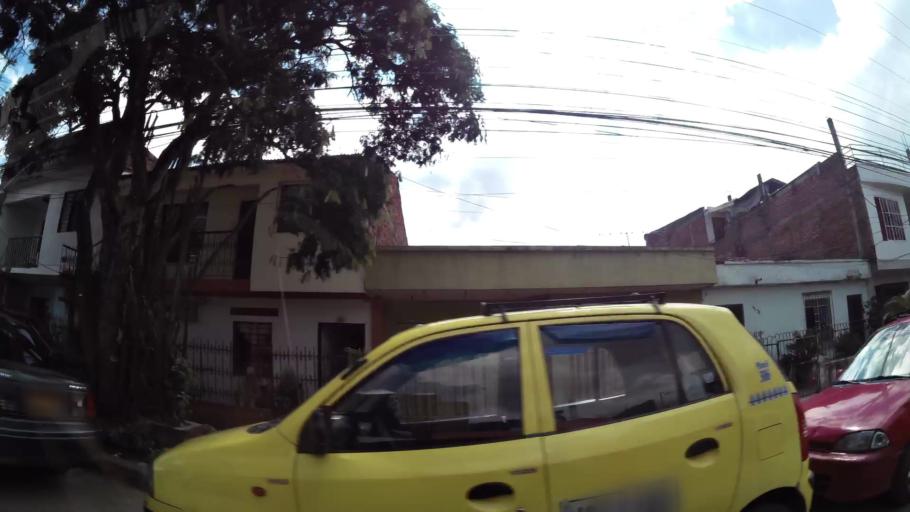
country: CO
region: Valle del Cauca
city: Cali
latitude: 3.4058
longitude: -76.5160
